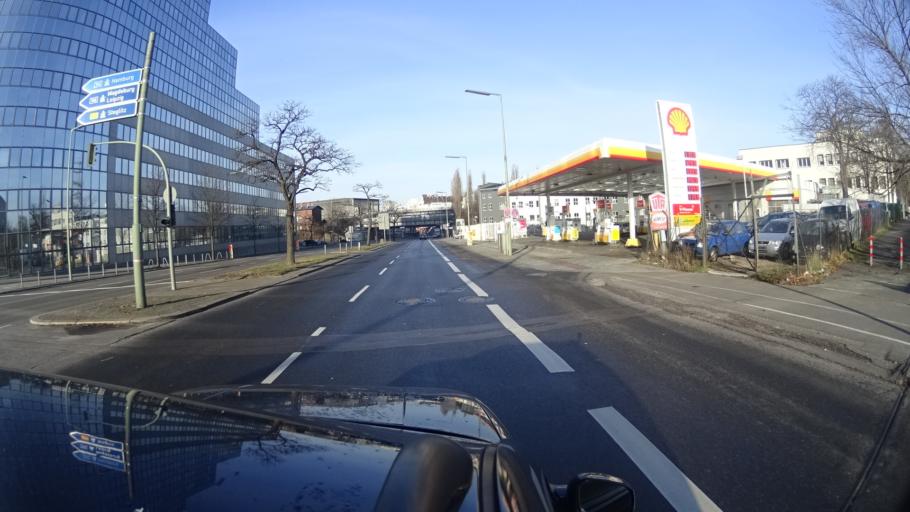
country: DE
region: Berlin
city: Berlin Schoeneberg
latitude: 52.4782
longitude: 13.3553
